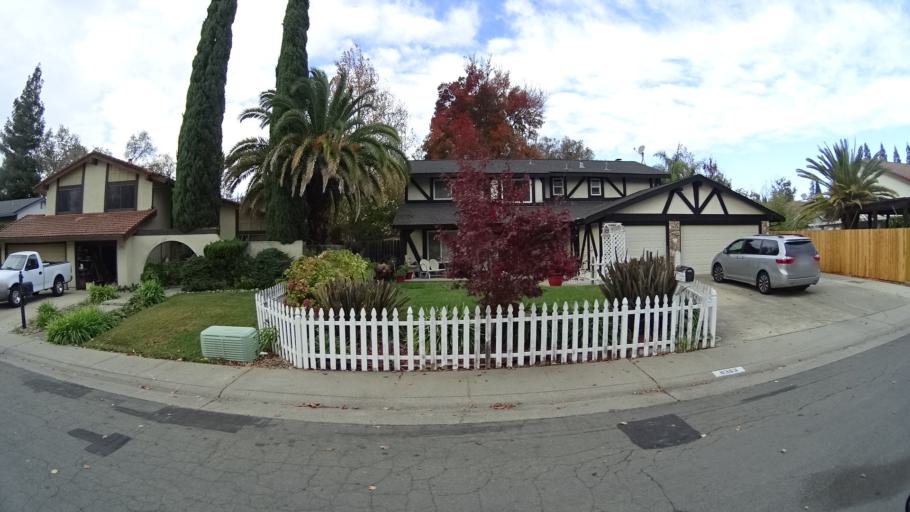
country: US
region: California
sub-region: Sacramento County
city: Citrus Heights
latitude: 38.7179
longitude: -121.2516
